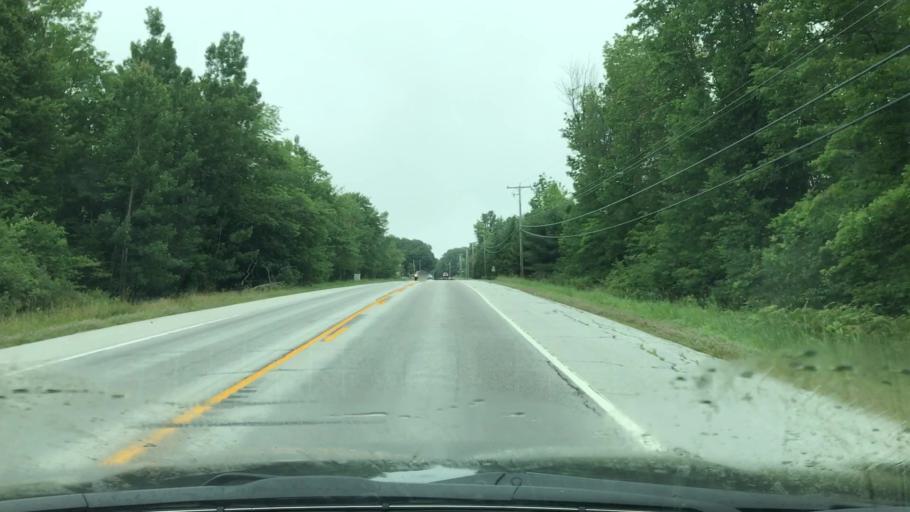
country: US
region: Maine
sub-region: Waldo County
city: Northport
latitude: 44.3261
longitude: -68.9603
